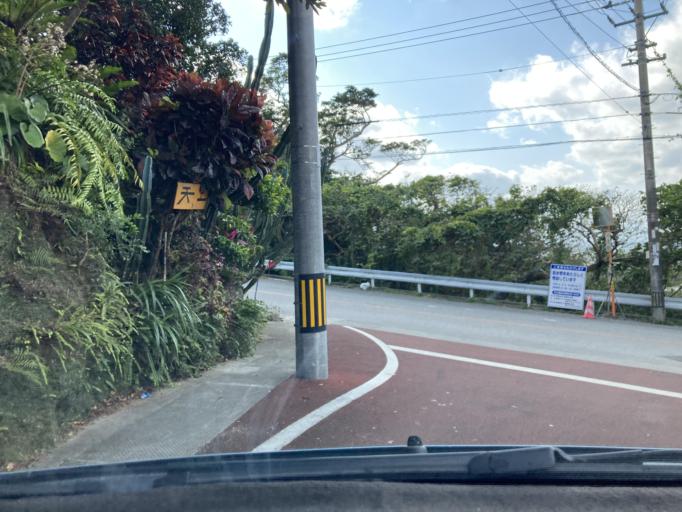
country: JP
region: Okinawa
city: Tomigusuku
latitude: 26.1845
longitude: 127.7591
